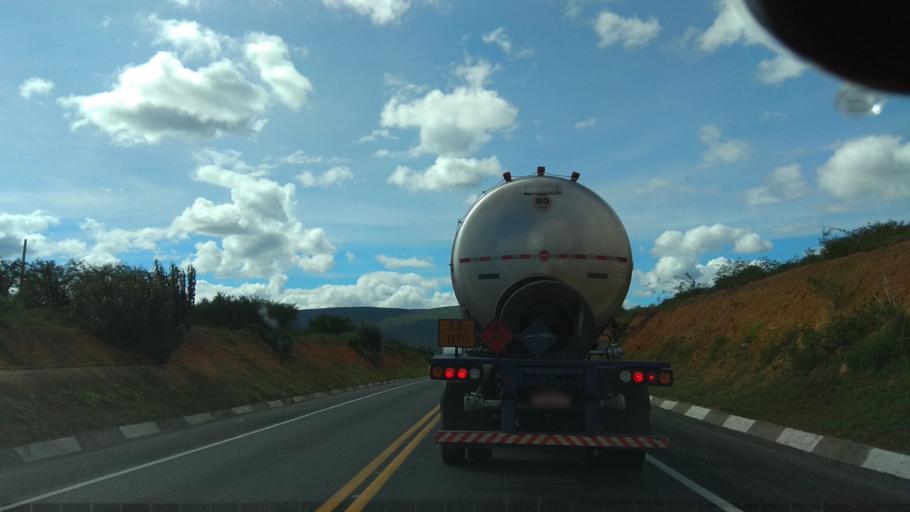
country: BR
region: Bahia
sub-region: Santa Ines
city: Santa Ines
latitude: -13.2798
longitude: -40.0169
